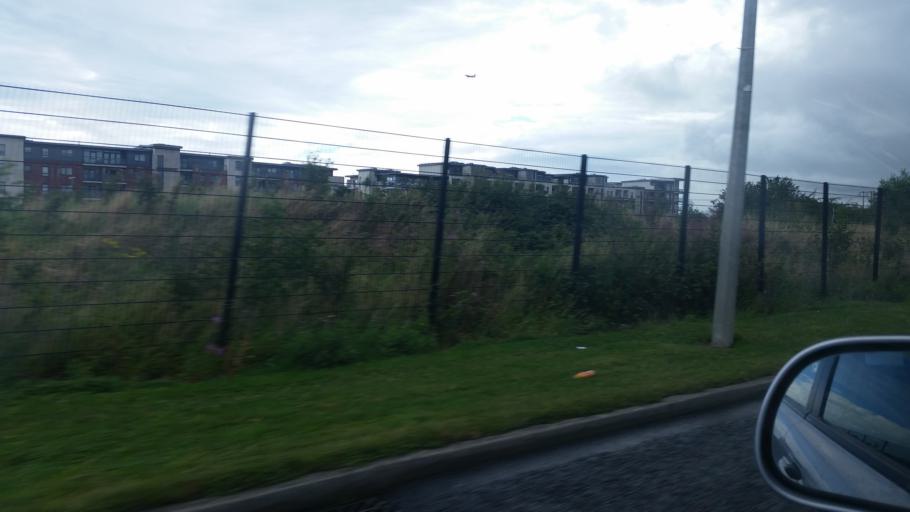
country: IE
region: Leinster
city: Donaghmede
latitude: 53.4023
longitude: -6.1743
